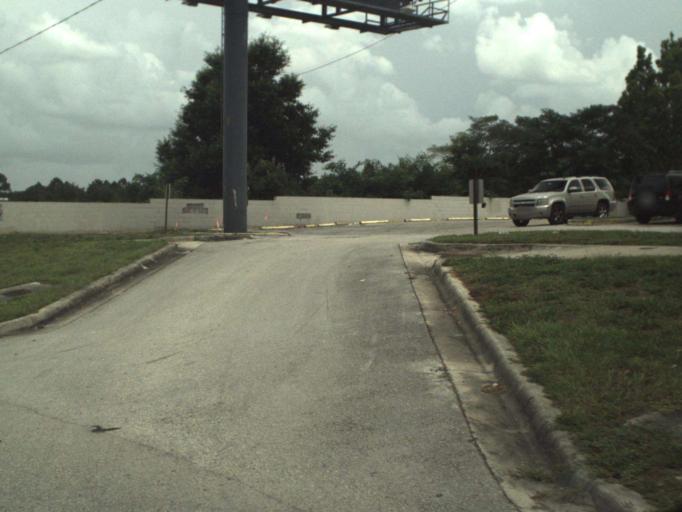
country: US
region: Florida
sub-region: Seminole County
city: Forest City
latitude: 28.6728
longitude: -81.4760
